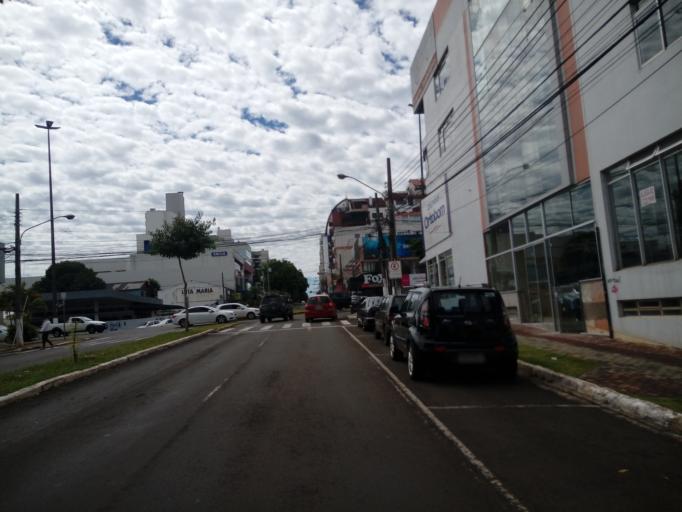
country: BR
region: Santa Catarina
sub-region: Chapeco
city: Chapeco
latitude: -27.0955
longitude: -52.6174
